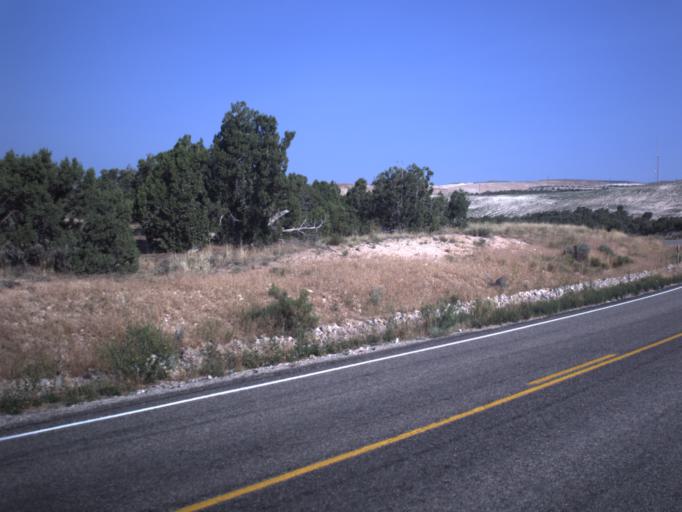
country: US
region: Utah
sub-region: Uintah County
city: Vernal
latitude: 40.6082
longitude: -109.4691
